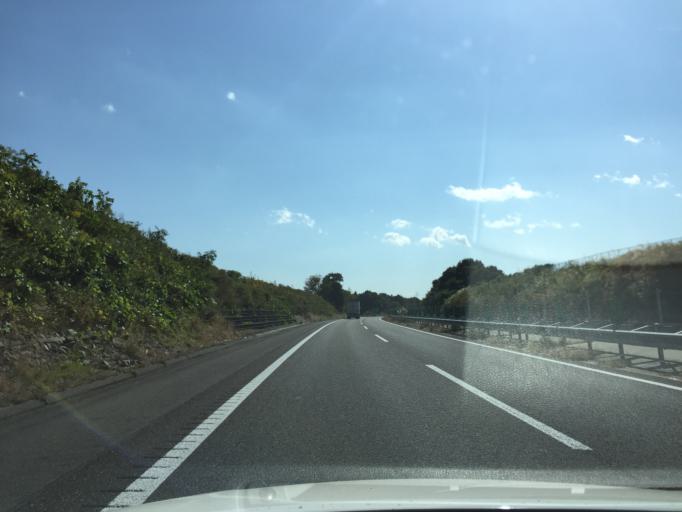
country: JP
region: Fukushima
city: Sukagawa
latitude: 37.3206
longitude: 140.3423
